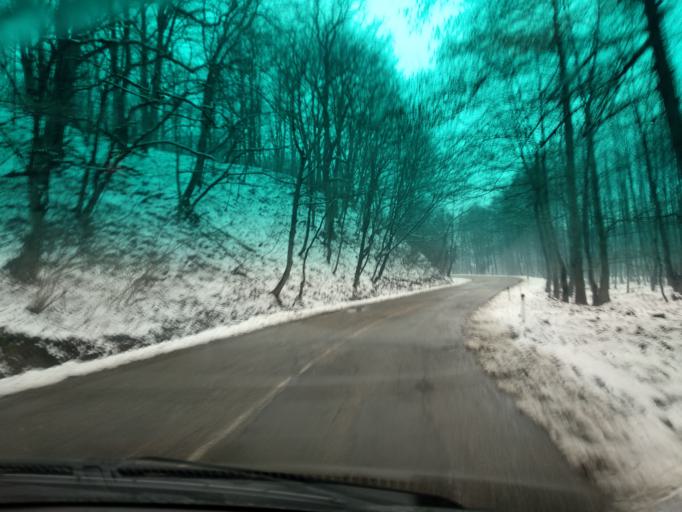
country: RU
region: Krasnodarskiy
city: Khadyzhensk
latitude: 44.2087
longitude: 39.4274
